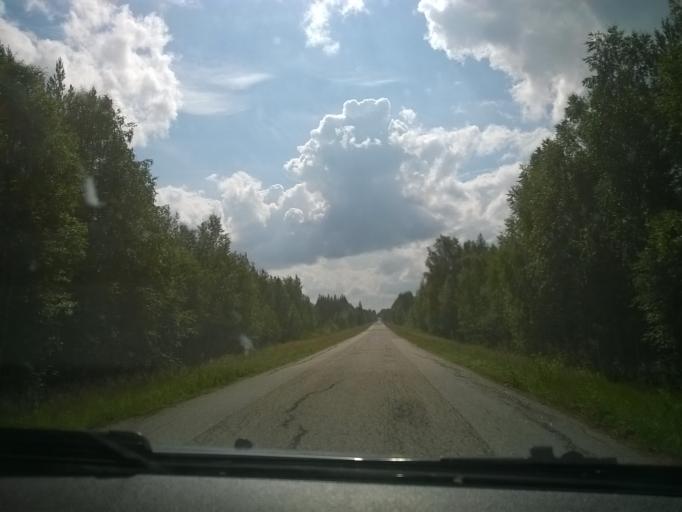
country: FI
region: Kainuu
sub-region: Kehys-Kainuu
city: Kuhmo
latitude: 64.4087
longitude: 29.7703
